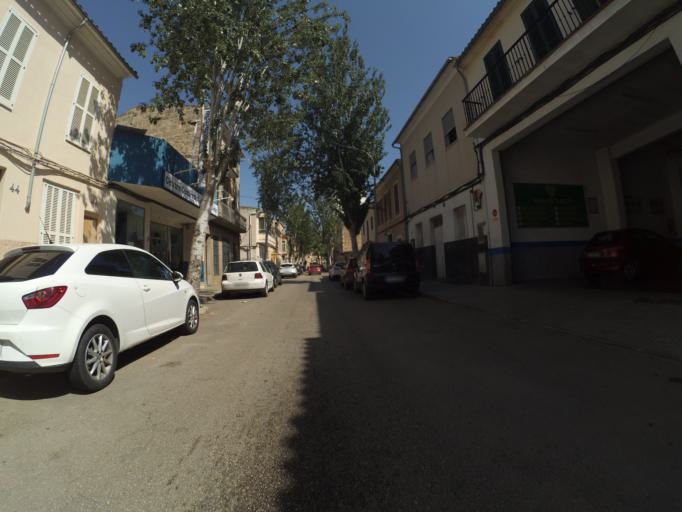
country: ES
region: Balearic Islands
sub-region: Illes Balears
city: Manacor
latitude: 39.5714
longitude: 3.2021
